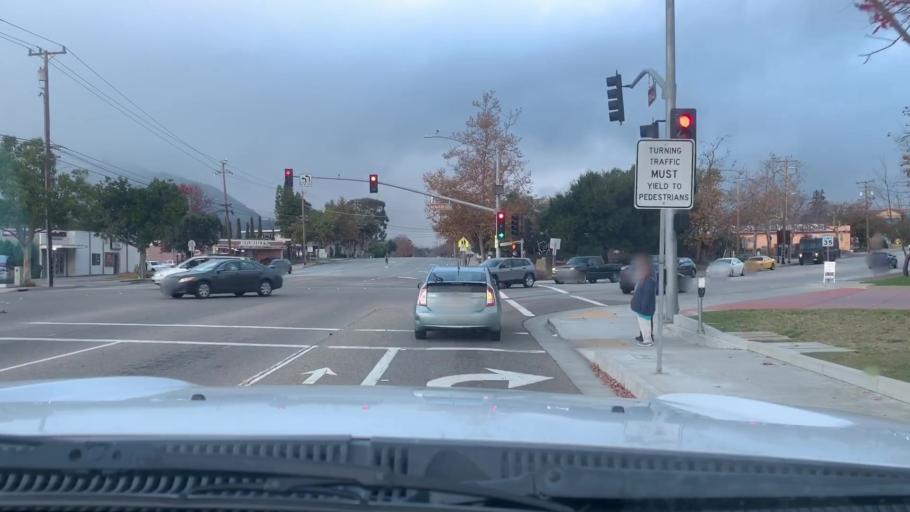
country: US
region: California
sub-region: San Luis Obispo County
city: San Luis Obispo
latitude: 35.2697
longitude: -120.6563
